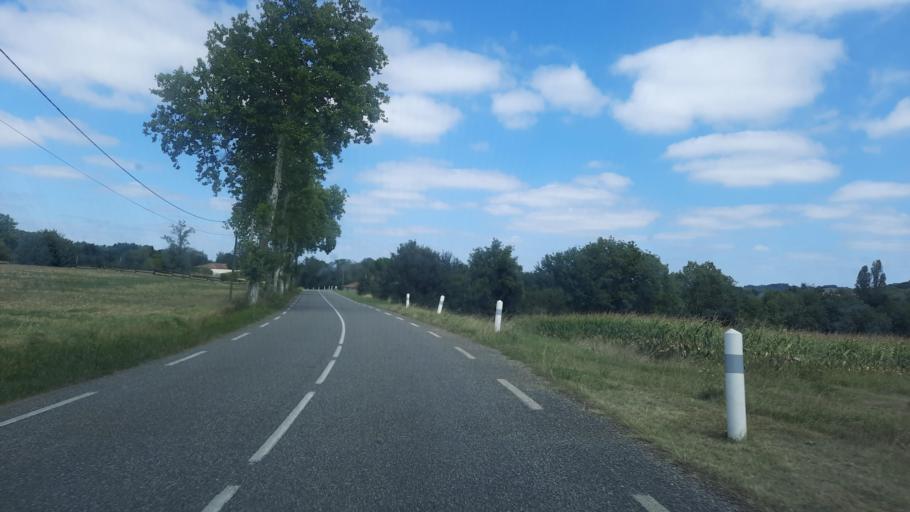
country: FR
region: Midi-Pyrenees
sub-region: Departement du Gers
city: Lombez
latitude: 43.3896
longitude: 0.7816
